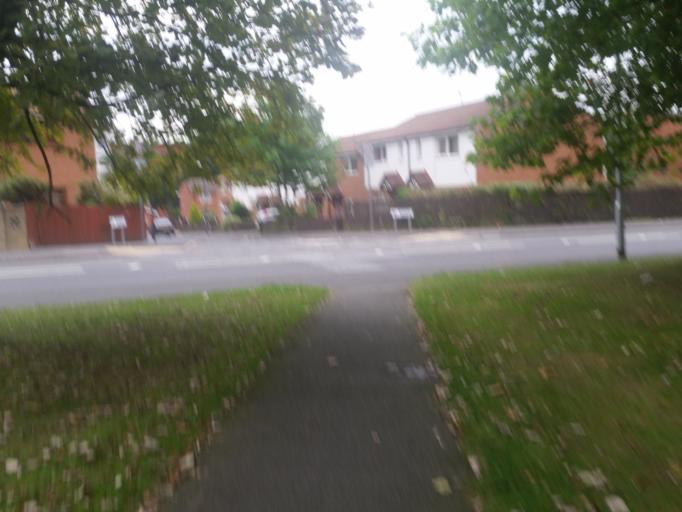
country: GB
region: England
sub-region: Manchester
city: Hulme
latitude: 53.4742
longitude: -2.2700
